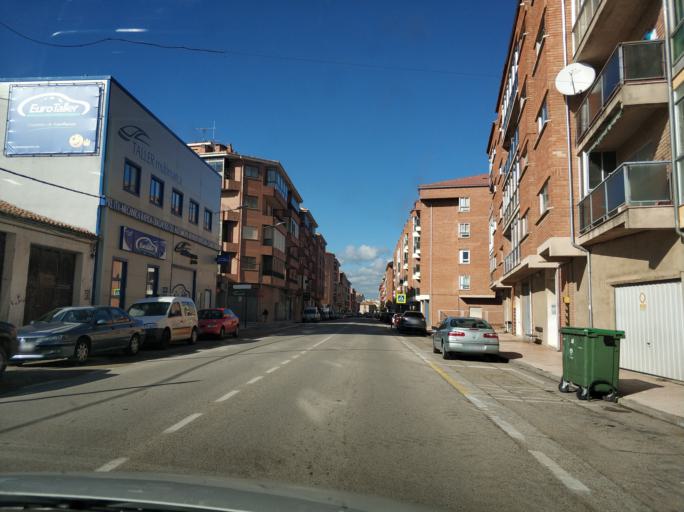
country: ES
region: Castille and Leon
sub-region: Provincia de Soria
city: Almazan
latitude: 41.4824
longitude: -2.5294
